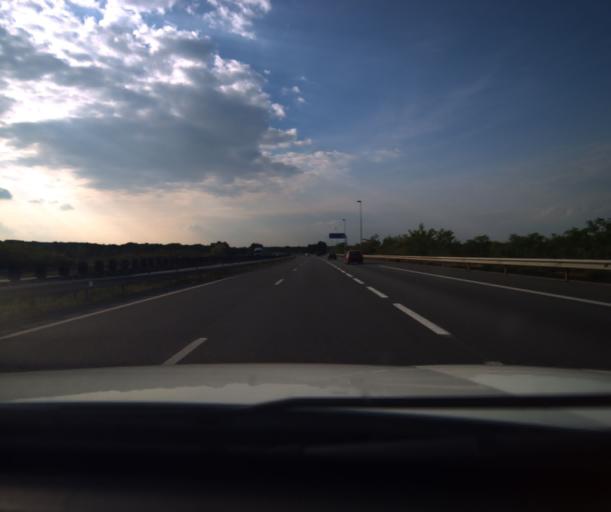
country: FR
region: Midi-Pyrenees
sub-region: Departement de la Haute-Garonne
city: Castelnau-d'Estretefonds
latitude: 43.8079
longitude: 1.3653
